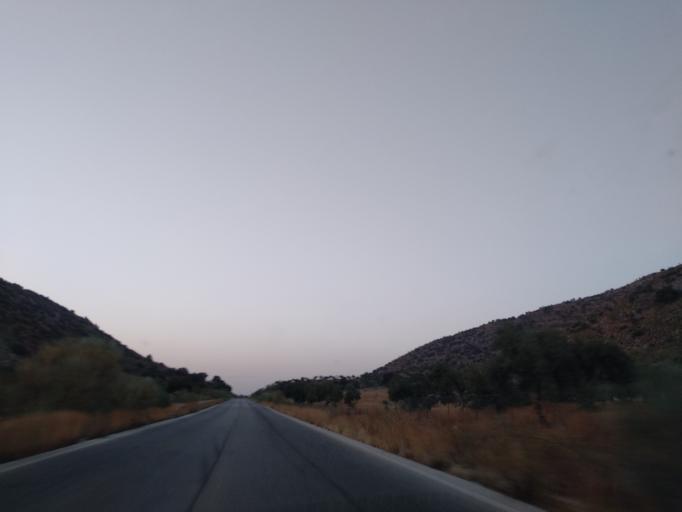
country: ES
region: Andalusia
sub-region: Provincia de Malaga
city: Cartama
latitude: 36.6908
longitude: -4.6509
